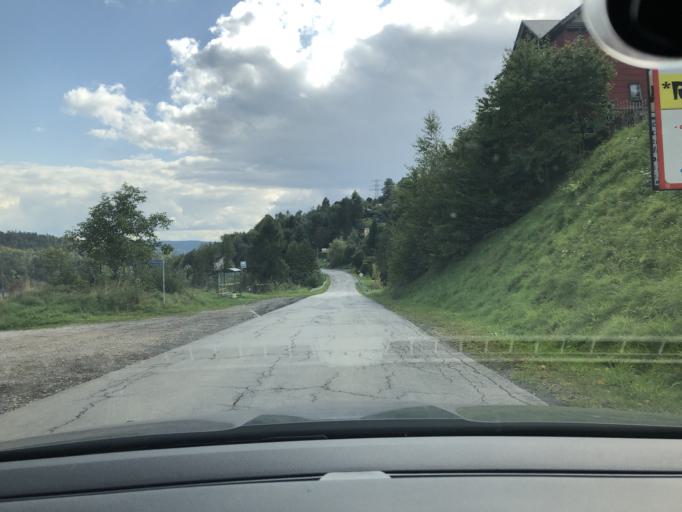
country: PL
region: Silesian Voivodeship
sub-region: Powiat zywiecki
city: Czernichow
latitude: 49.7399
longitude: 19.2059
